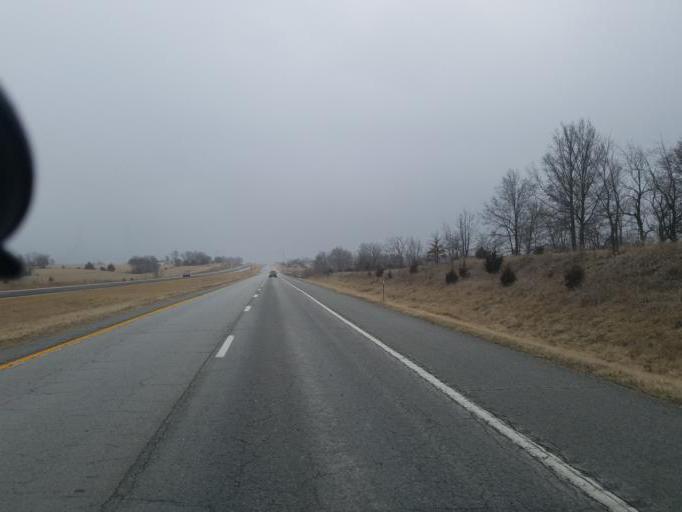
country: US
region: Missouri
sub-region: Macon County
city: La Plata
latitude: 39.9079
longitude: -92.4733
